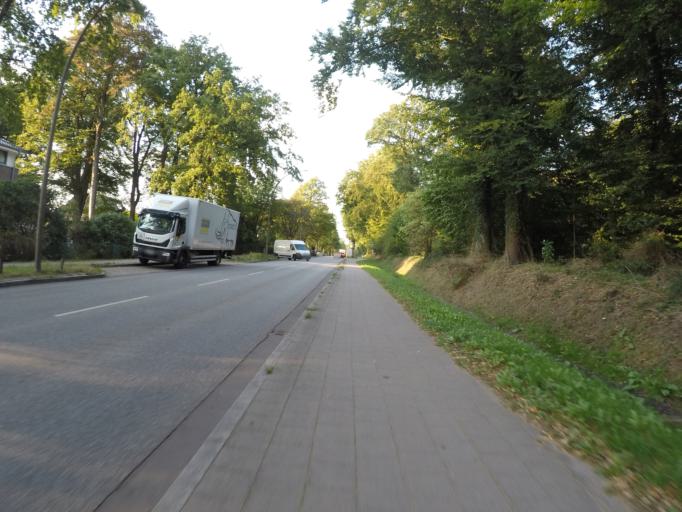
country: DE
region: Hamburg
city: Bergstedt
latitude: 53.6430
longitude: 10.1585
